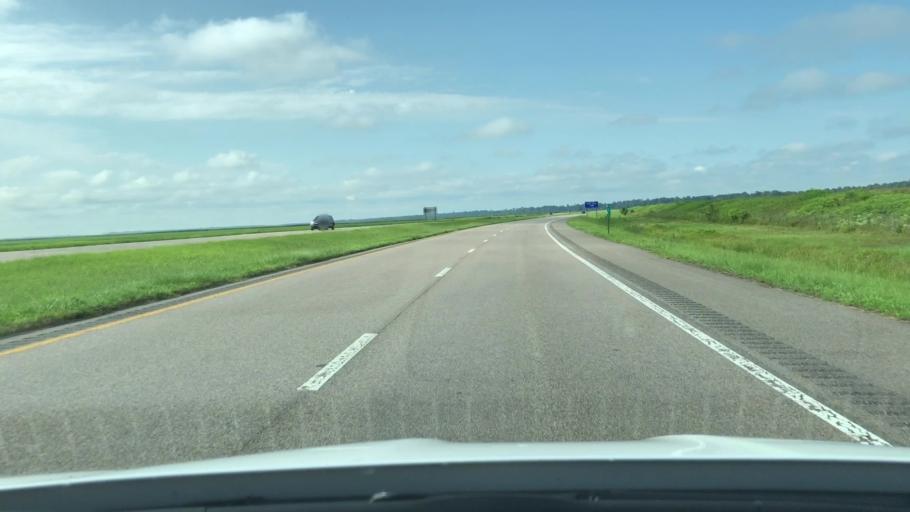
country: US
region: North Carolina
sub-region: Currituck County
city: Moyock
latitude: 36.5943
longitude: -76.3788
